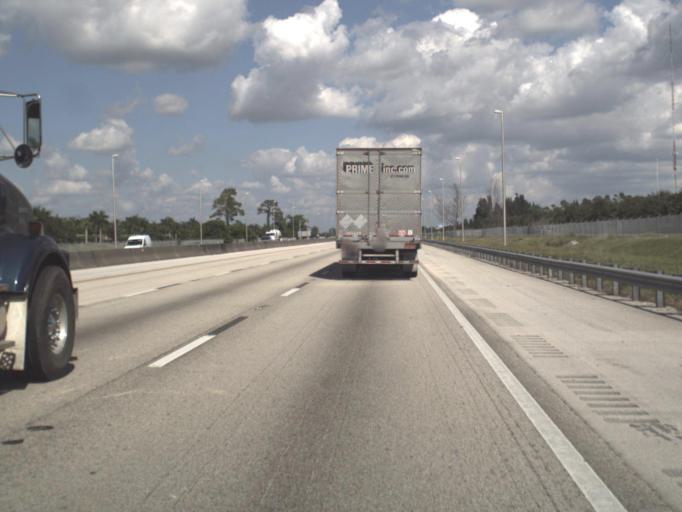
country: US
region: Florida
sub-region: Palm Beach County
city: Villages of Oriole
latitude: 26.5113
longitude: -80.1725
